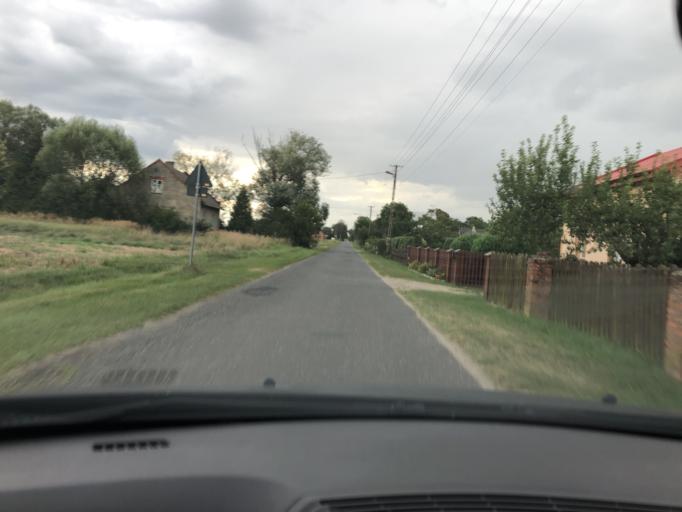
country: PL
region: Lodz Voivodeship
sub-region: Powiat wieruszowski
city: Czastary
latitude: 51.2410
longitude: 18.2866
